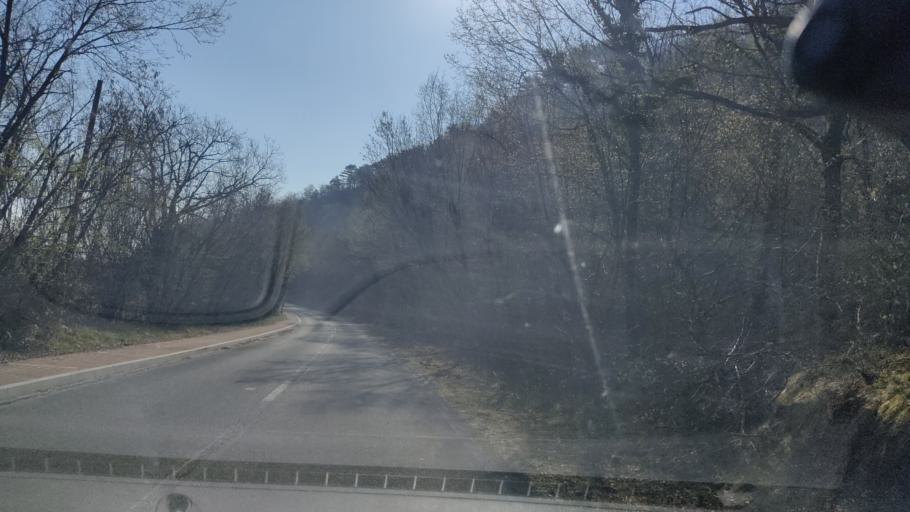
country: IT
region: Friuli Venezia Giulia
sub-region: Provincia di Pordenone
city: Budoia
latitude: 46.0585
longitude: 12.5237
